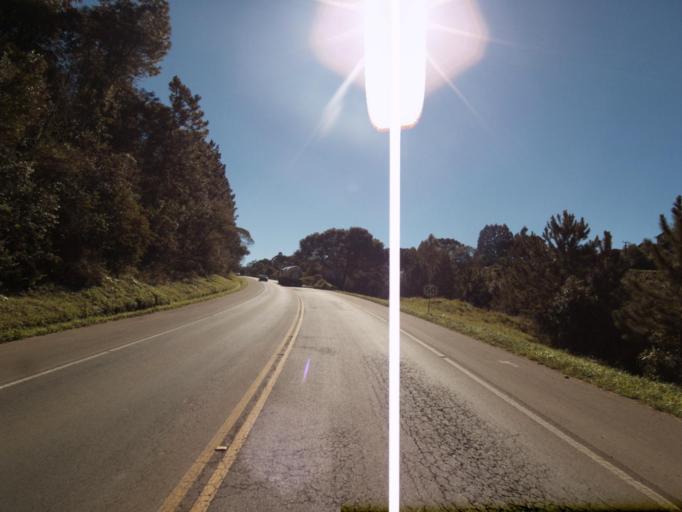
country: BR
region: Santa Catarina
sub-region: Joacaba
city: Joacaba
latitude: -27.0775
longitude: -51.6629
